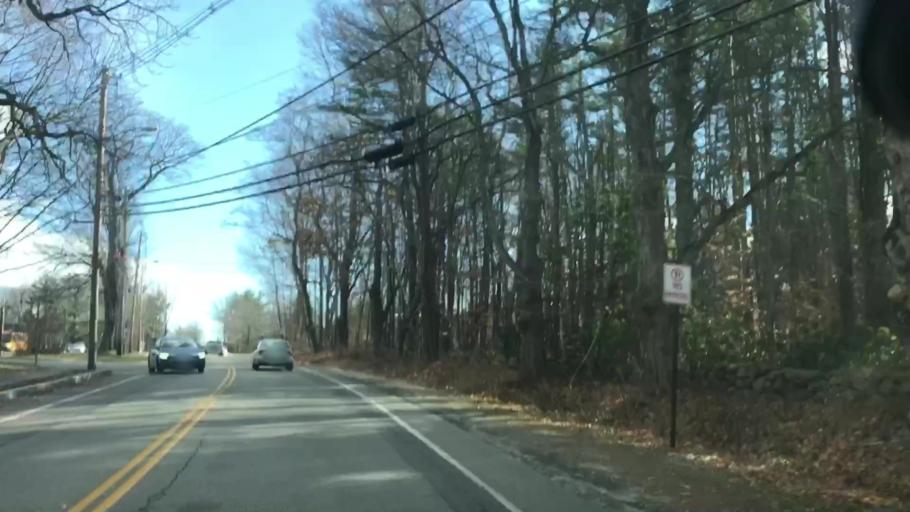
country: US
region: New Hampshire
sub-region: Carroll County
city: Wolfeboro
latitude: 43.5754
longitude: -71.1913
